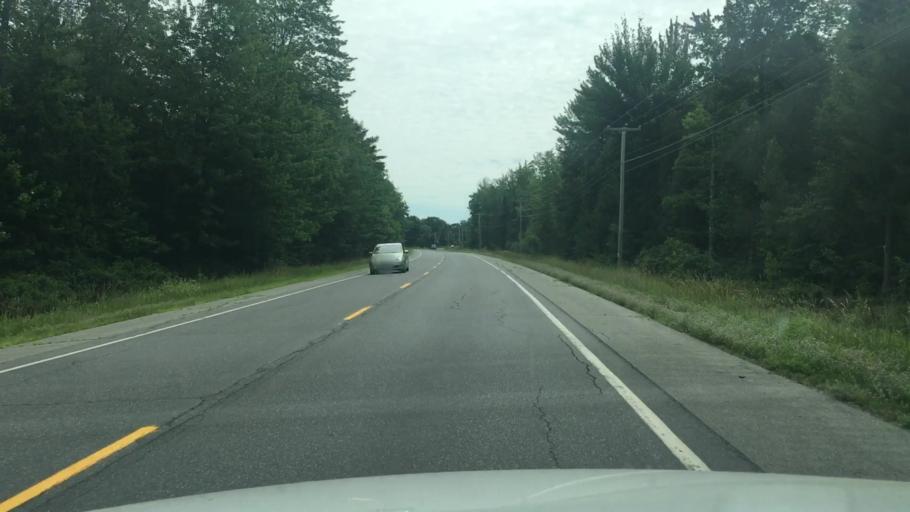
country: US
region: Maine
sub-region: Waldo County
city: Burnham
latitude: 44.6131
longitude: -69.3627
